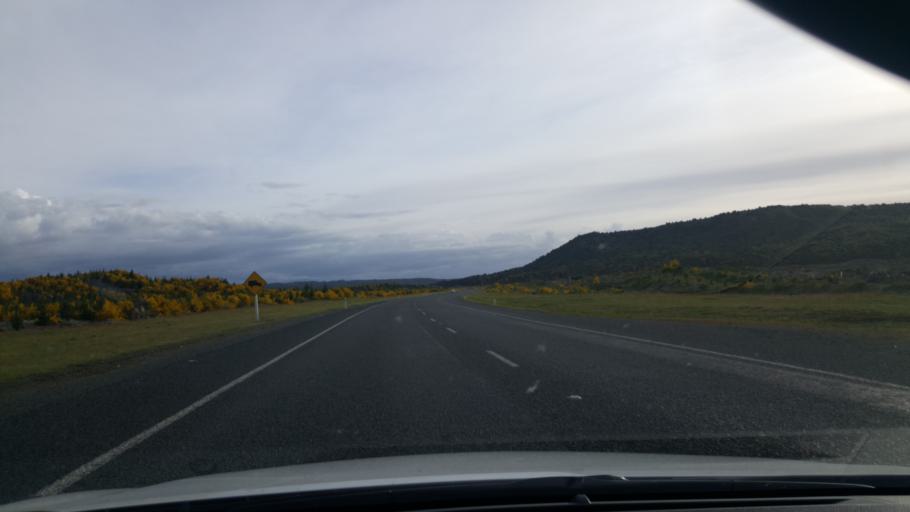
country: NZ
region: Waikato
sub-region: Taupo District
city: Taupo
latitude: -38.8392
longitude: 176.0637
